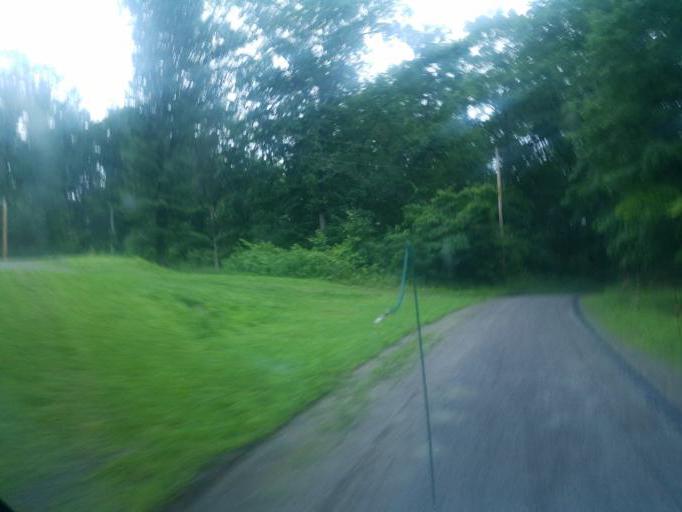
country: US
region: Ohio
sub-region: Columbiana County
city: Salineville
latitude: 40.6214
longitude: -80.8965
